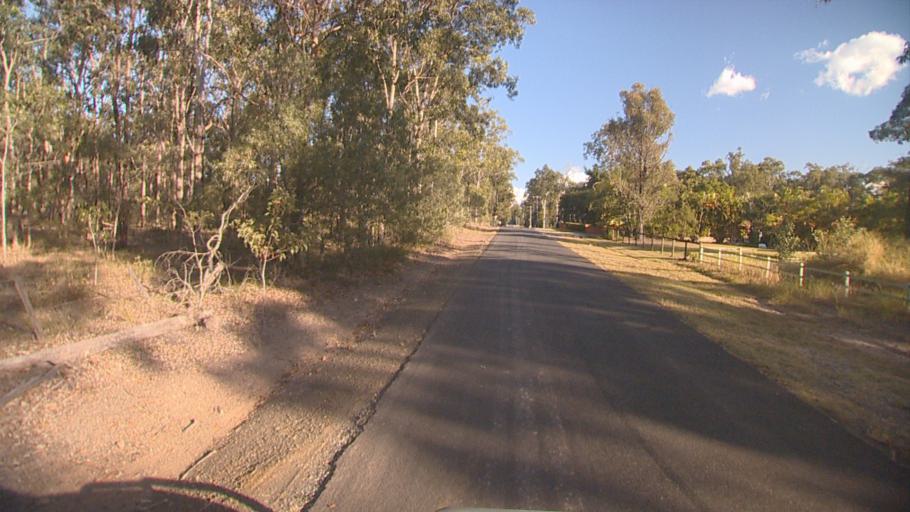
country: AU
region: Queensland
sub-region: Ipswich
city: Springfield Lakes
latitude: -27.6947
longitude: 152.9496
